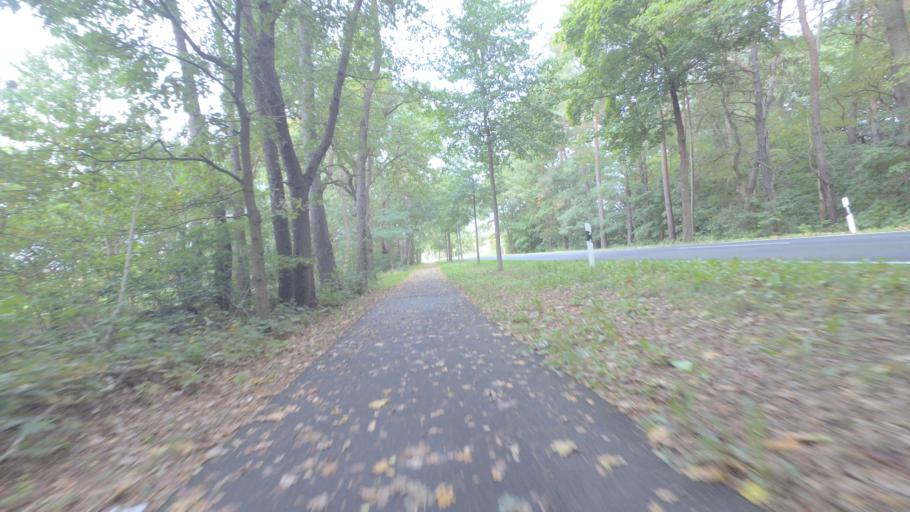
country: DE
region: Brandenburg
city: Luckenwalde
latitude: 52.1586
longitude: 13.1843
